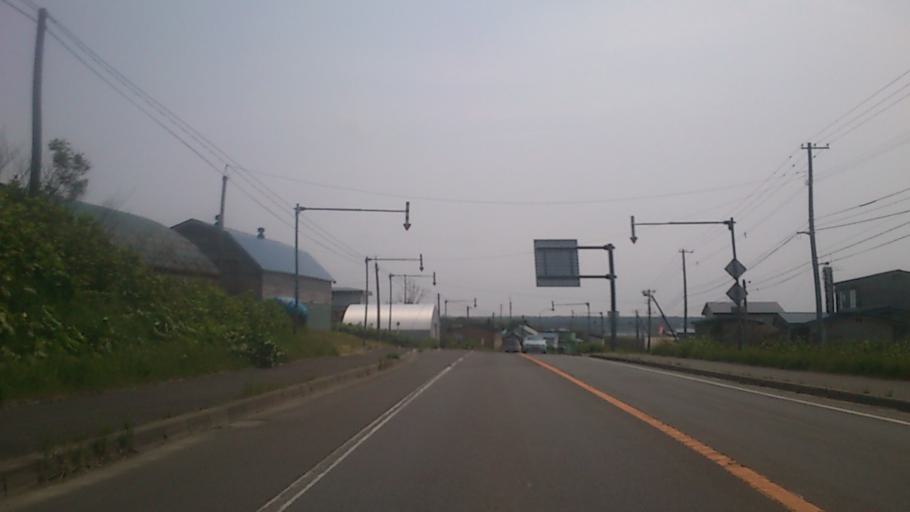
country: JP
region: Hokkaido
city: Nemuro
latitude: 43.2802
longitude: 145.5064
